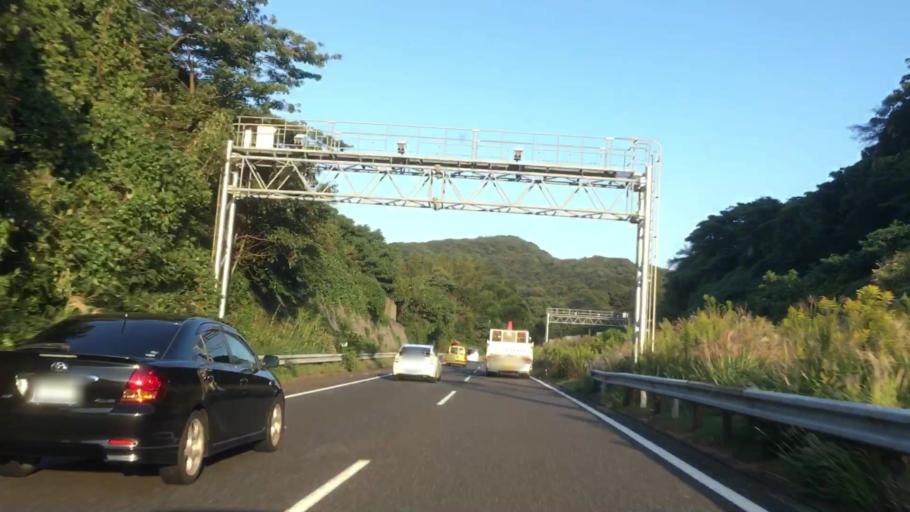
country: JP
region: Yamaguchi
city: Shimonoseki
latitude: 33.9516
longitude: 130.9861
